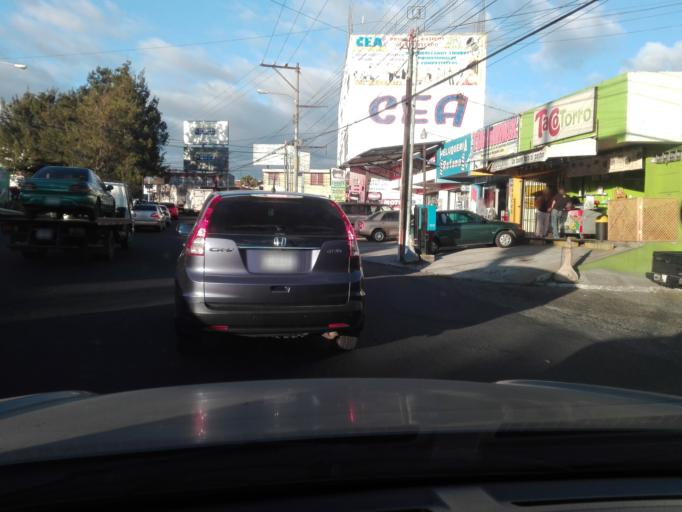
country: GT
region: Guatemala
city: Mixco
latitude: 14.5903
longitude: -90.5786
